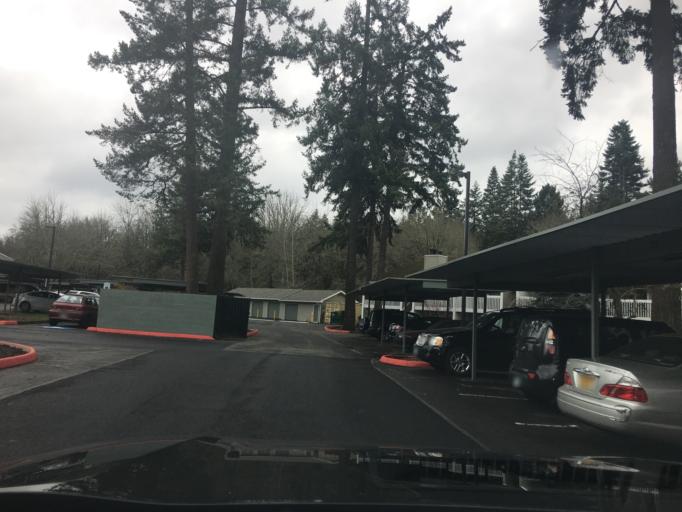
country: US
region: Oregon
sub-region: Washington County
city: Aloha
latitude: 45.4964
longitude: -122.8481
